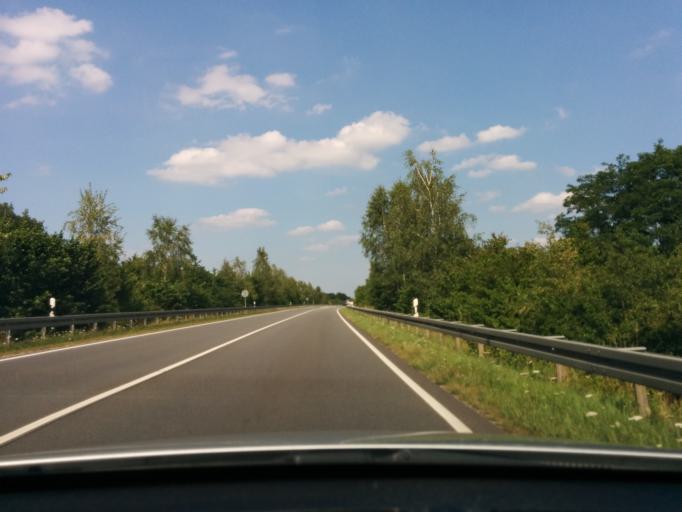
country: DE
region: North Rhine-Westphalia
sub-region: Regierungsbezirk Munster
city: Neuenkirchen
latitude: 52.2257
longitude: 7.3789
